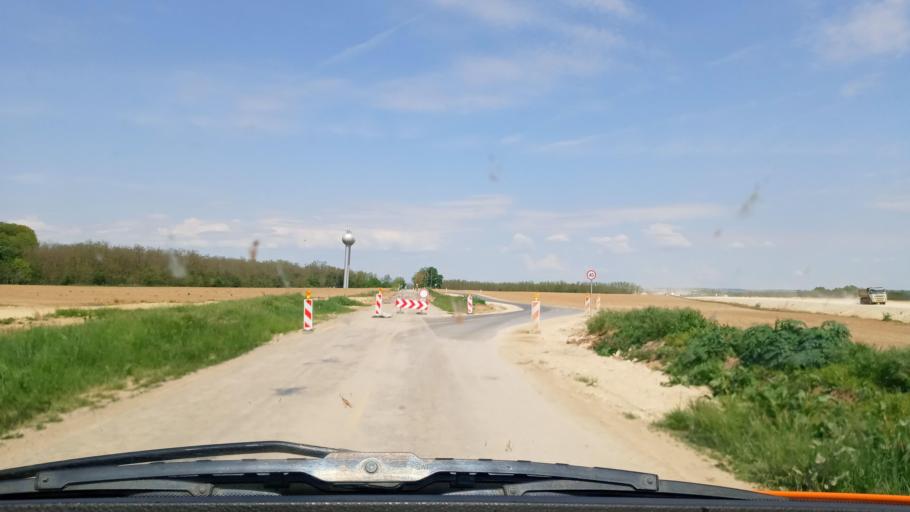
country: HU
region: Baranya
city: Boly
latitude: 45.8917
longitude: 18.5612
